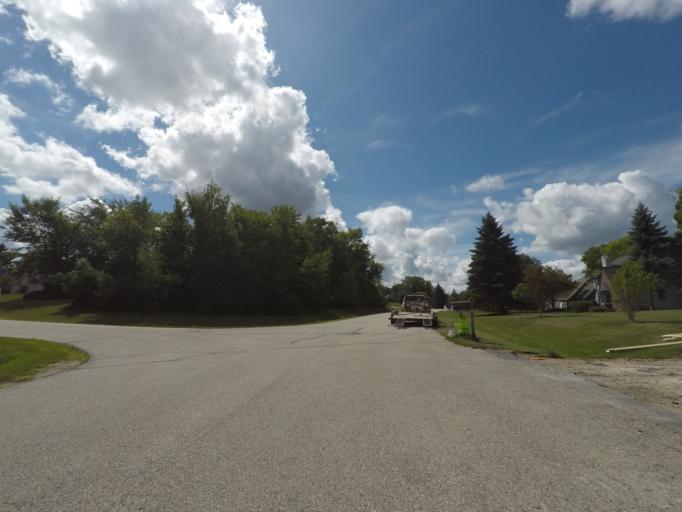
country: US
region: Wisconsin
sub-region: Waukesha County
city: Pewaukee
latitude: 43.0564
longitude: -88.3066
